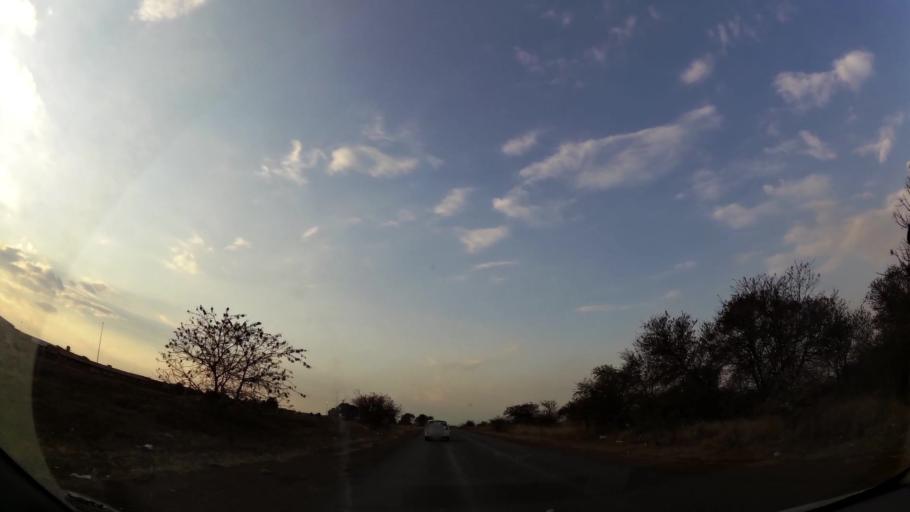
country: ZA
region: Gauteng
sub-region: City of Johannesburg Metropolitan Municipality
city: Orange Farm
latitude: -26.5783
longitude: 27.8570
